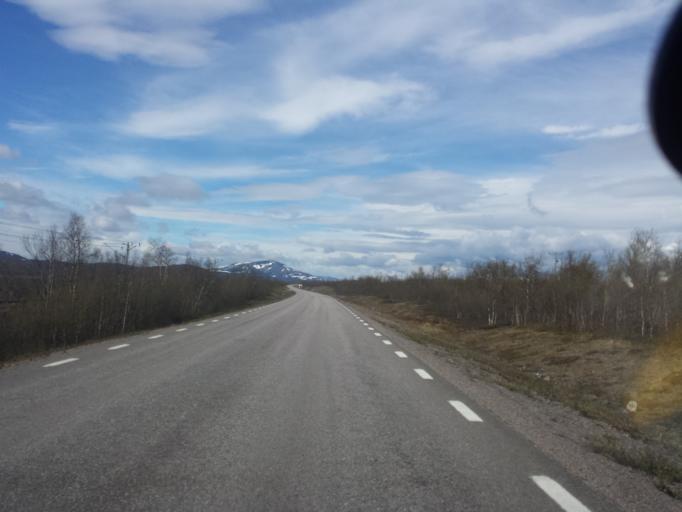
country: SE
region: Norrbotten
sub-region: Kiruna Kommun
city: Kiruna
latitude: 68.0525
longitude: 19.8298
